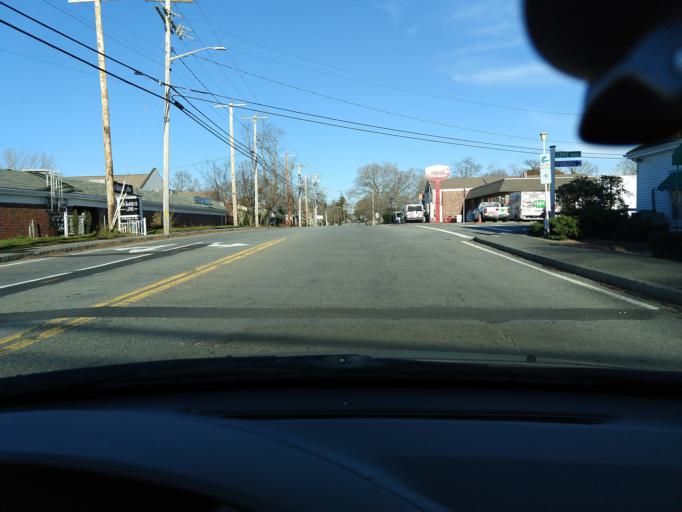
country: US
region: Massachusetts
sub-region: Barnstable County
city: Orleans
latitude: 41.7881
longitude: -69.9915
